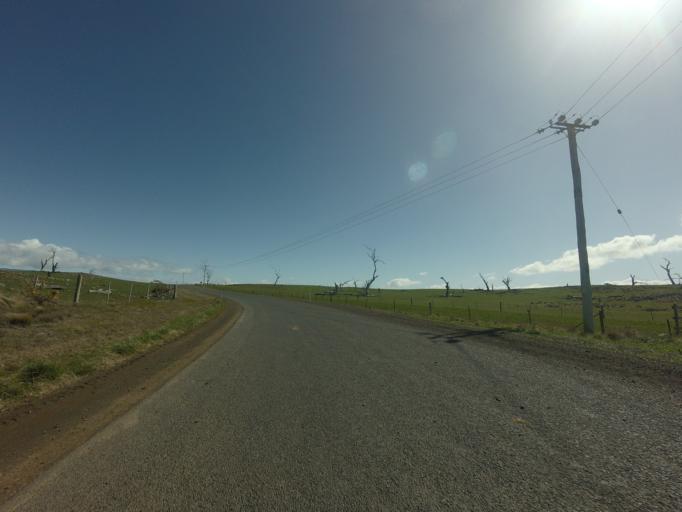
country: AU
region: Tasmania
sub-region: Northern Midlands
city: Evandale
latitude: -41.8960
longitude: 147.4334
